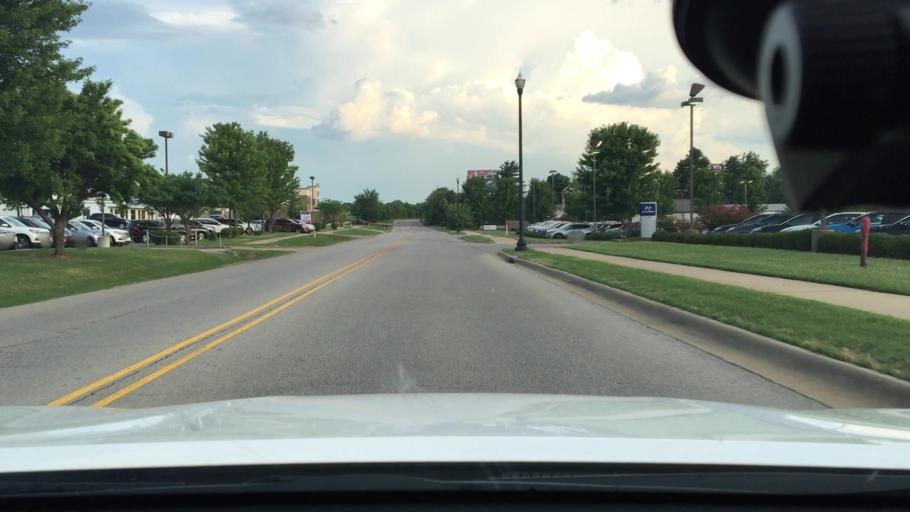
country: US
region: Arkansas
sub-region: Benton County
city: Bentonville
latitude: 36.3399
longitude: -94.1839
